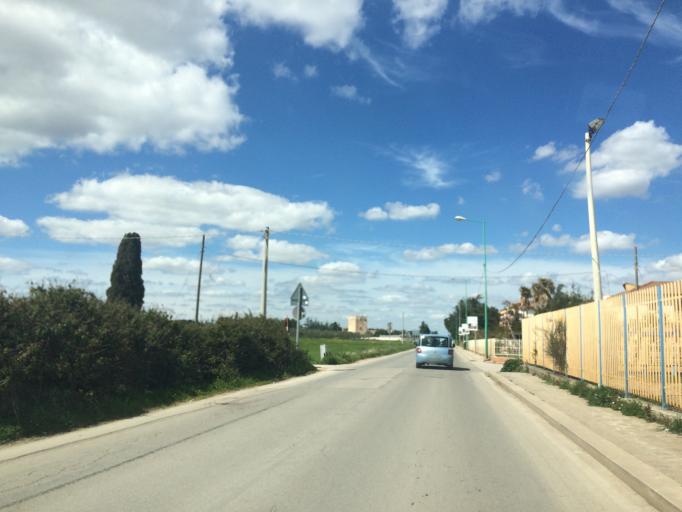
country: IT
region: Apulia
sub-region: Provincia di Bari
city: Terlizzi
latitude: 41.1264
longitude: 16.5393
